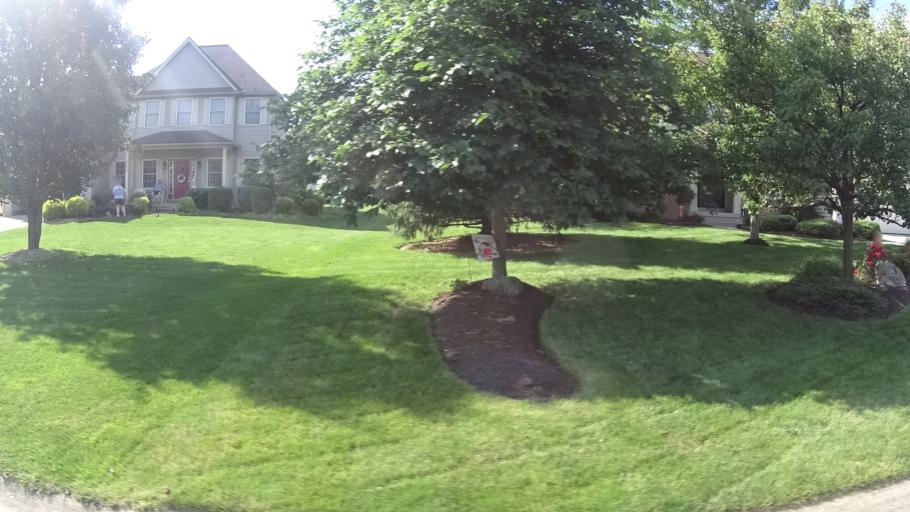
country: US
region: Ohio
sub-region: Erie County
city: Huron
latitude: 41.3817
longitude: -82.5214
